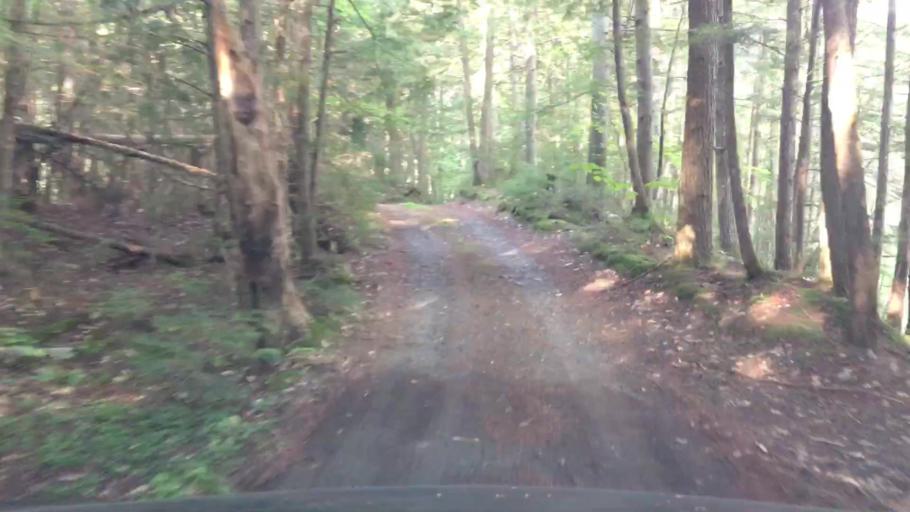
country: US
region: New Hampshire
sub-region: Grafton County
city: Littleton
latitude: 44.3042
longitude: -71.8930
